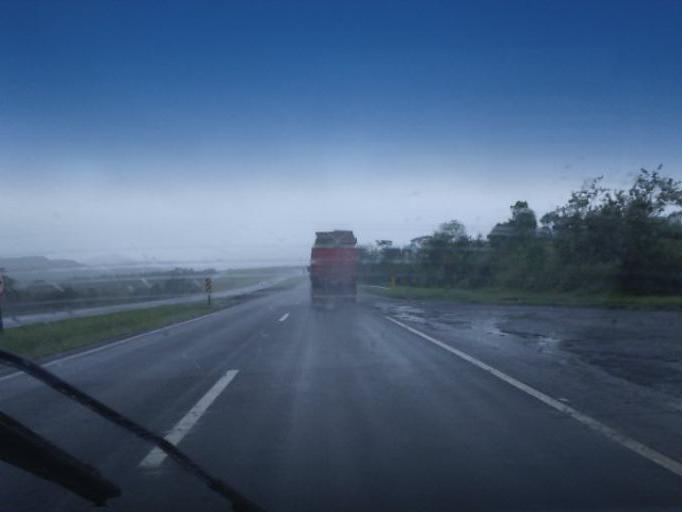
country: BR
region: Sao Paulo
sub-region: Cajati
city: Cajati
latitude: -24.9356
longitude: -48.2904
